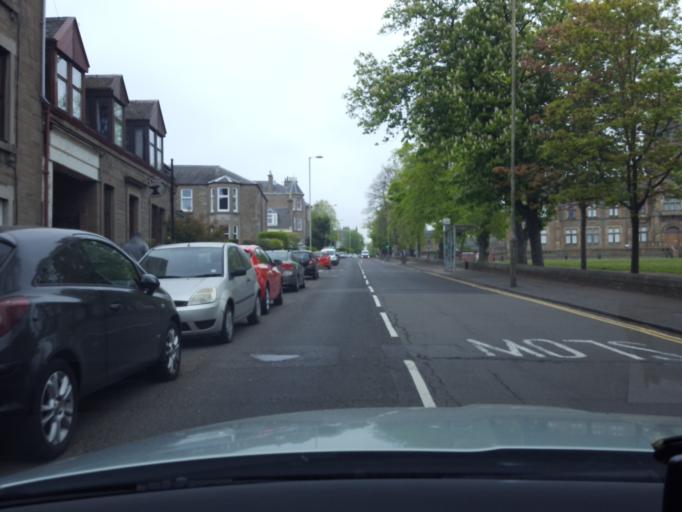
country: GB
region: Scotland
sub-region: Dundee City
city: Dundee
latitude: 56.4736
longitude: -2.9559
